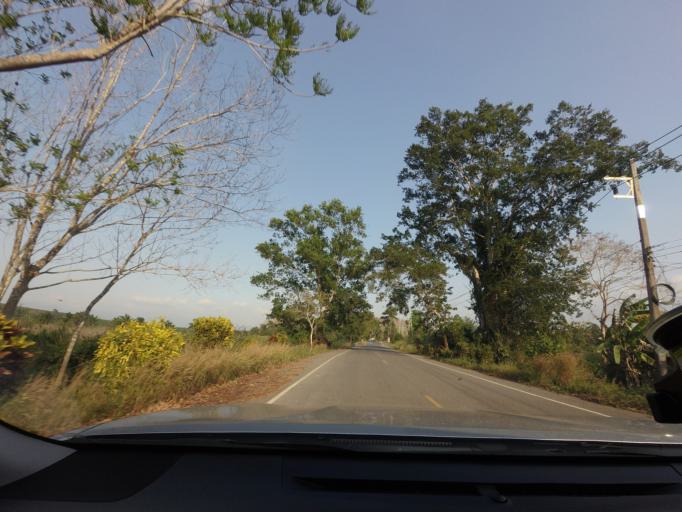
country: TH
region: Surat Thani
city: Phrasaeng
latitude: 8.5658
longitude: 99.2862
